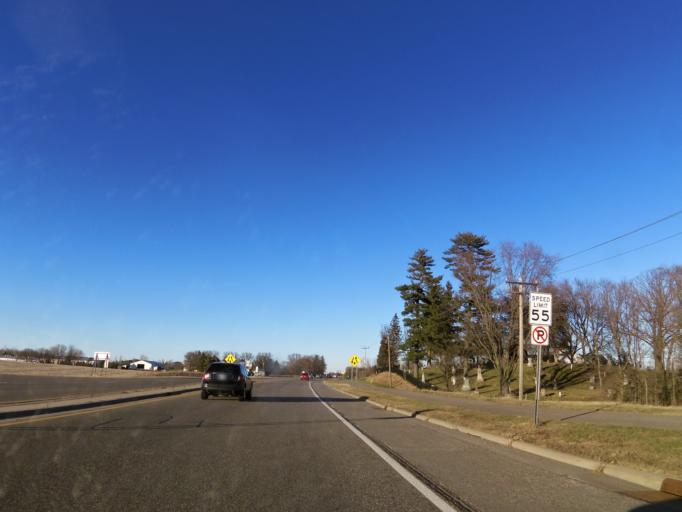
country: US
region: Minnesota
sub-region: Washington County
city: Grant
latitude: 45.0585
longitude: -92.8631
